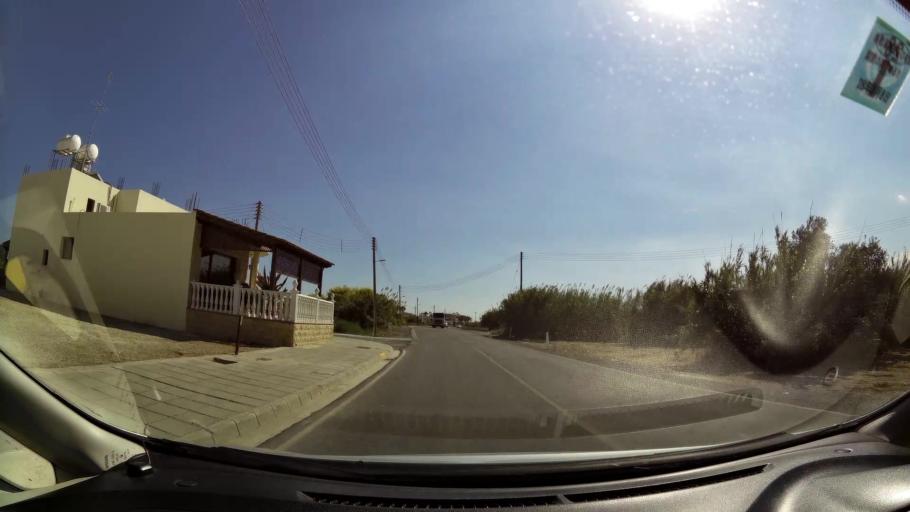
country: CY
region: Larnaka
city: Livadia
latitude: 34.9532
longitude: 33.6214
